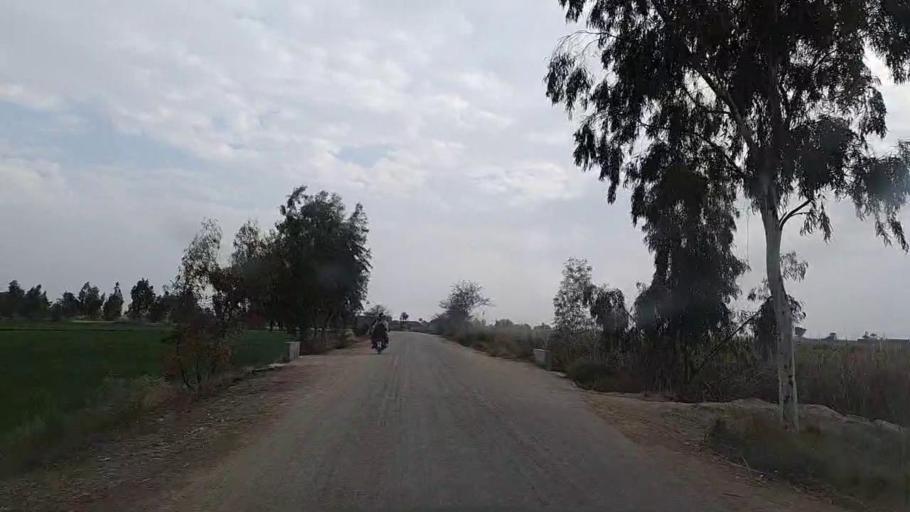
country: PK
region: Sindh
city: Sanghar
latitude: 26.2280
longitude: 69.0215
